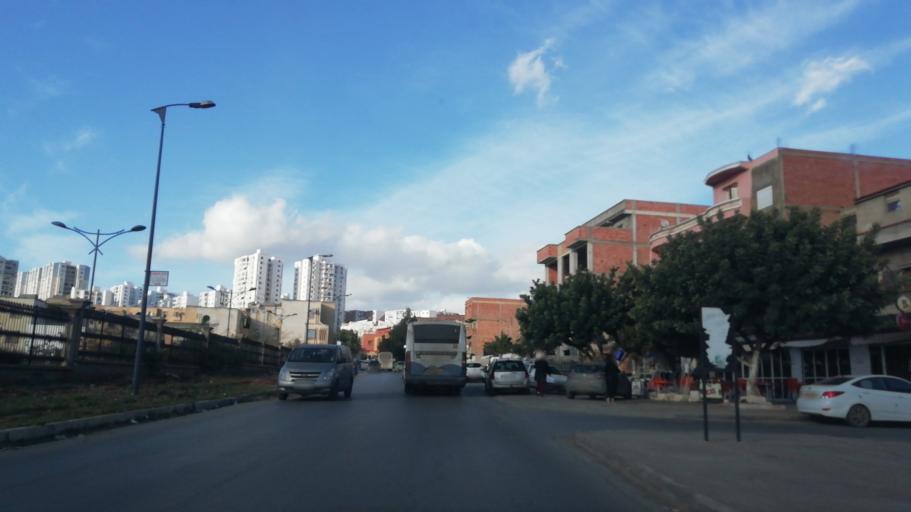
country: DZ
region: Oran
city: Bir el Djir
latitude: 35.6966
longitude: -0.5741
